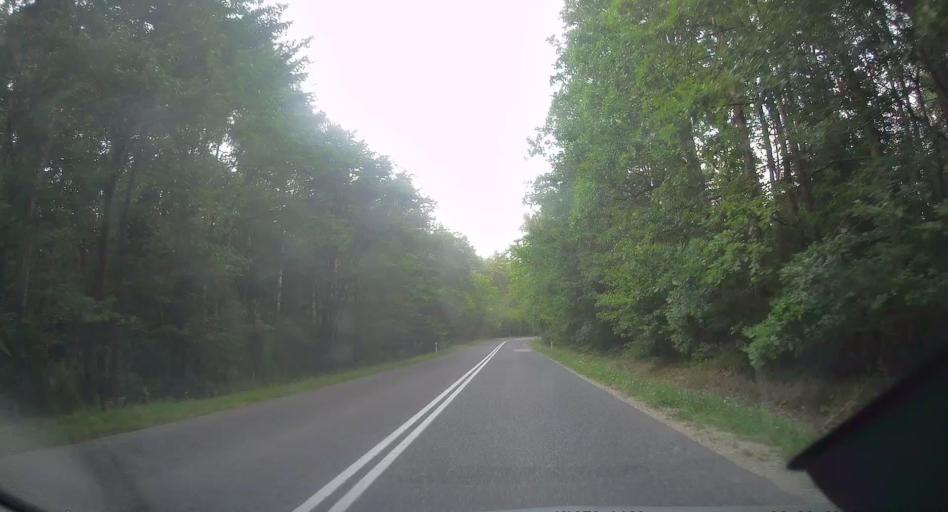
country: PL
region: Swietokrzyskie
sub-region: Powiat kielecki
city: Lopuszno
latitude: 50.8867
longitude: 20.2599
